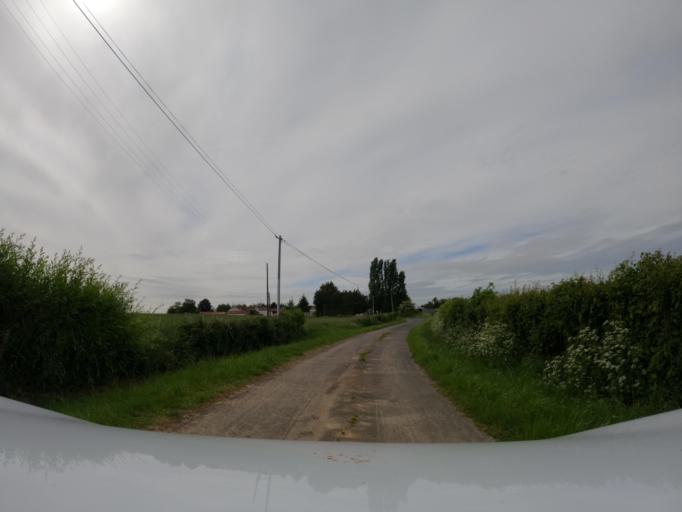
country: FR
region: Pays de la Loire
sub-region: Departement de la Vendee
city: Saint-Hilaire-des-Loges
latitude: 46.5027
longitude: -0.6386
